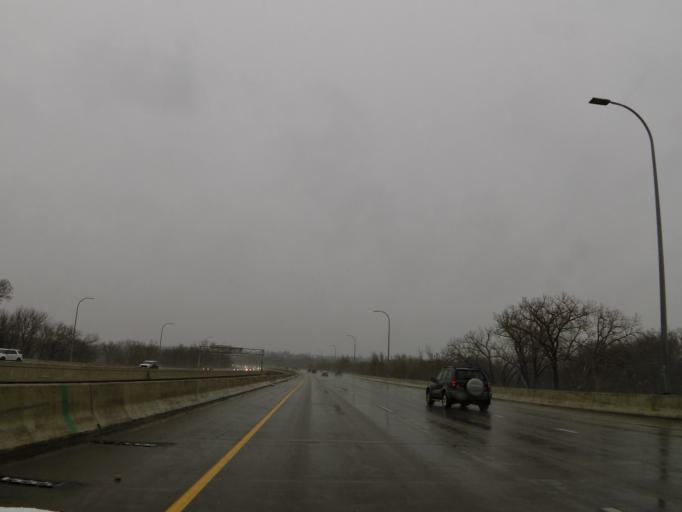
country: US
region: Minnesota
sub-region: Scott County
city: Savage
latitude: 44.7933
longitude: -93.4036
